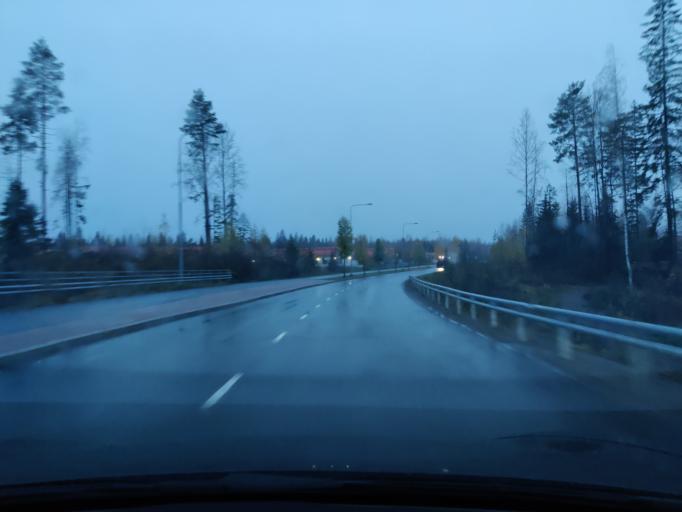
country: FI
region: Northern Savo
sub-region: Kuopio
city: Kuopio
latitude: 62.8273
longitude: 27.7003
